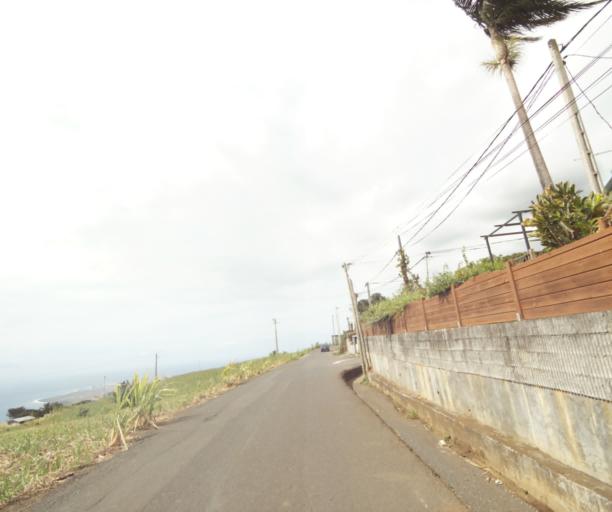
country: RE
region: Reunion
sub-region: Reunion
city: Saint-Paul
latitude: -21.0341
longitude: 55.2901
